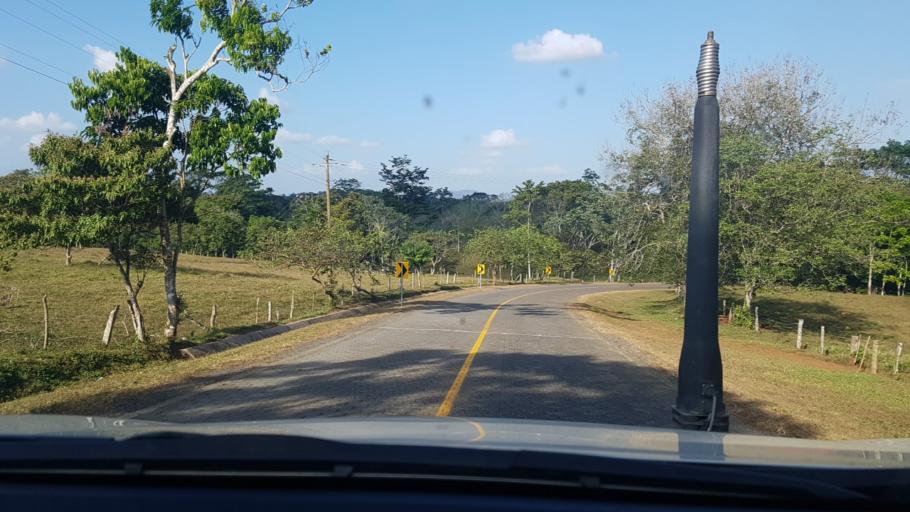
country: NI
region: Atlantico Sur
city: Nueva Guinea
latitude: 11.6947
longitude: -84.4132
